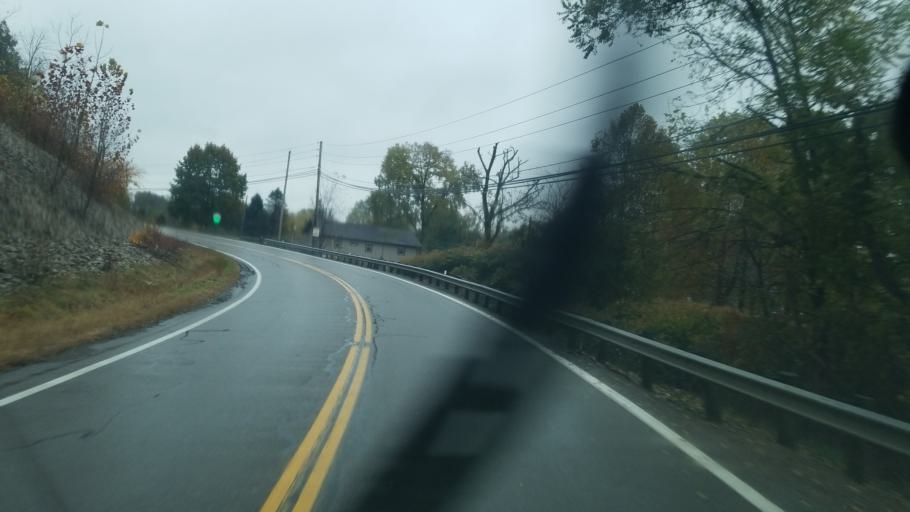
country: US
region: Ohio
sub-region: Coshocton County
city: Coshocton
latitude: 40.2915
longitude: -81.8726
